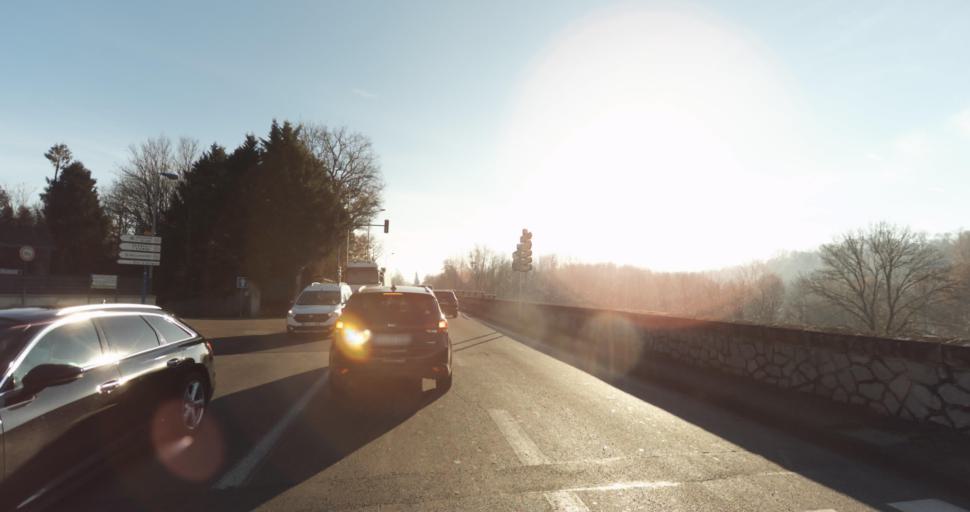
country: FR
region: Limousin
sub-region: Departement de la Haute-Vienne
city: Aixe-sur-Vienne
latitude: 45.7958
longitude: 1.1486
